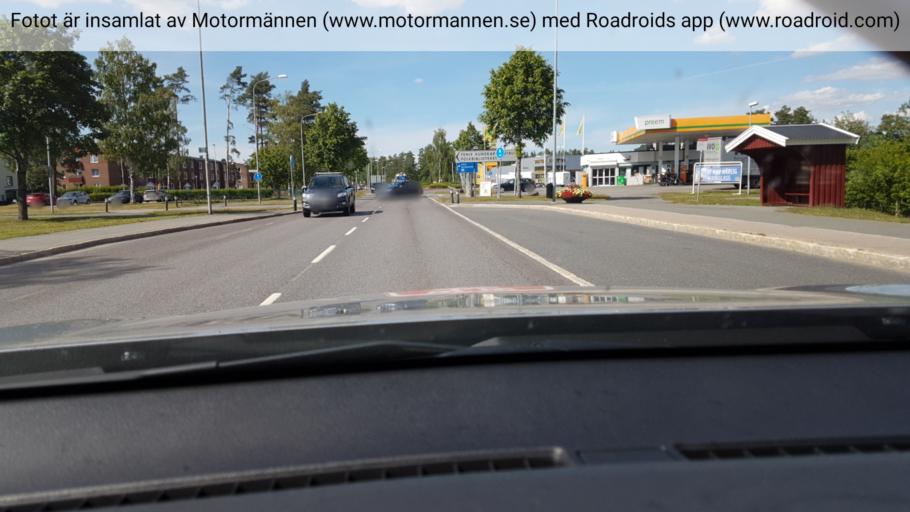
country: SE
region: Joenkoeping
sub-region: Vaggeryds Kommun
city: Vaggeryd
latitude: 57.5046
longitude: 14.1432
